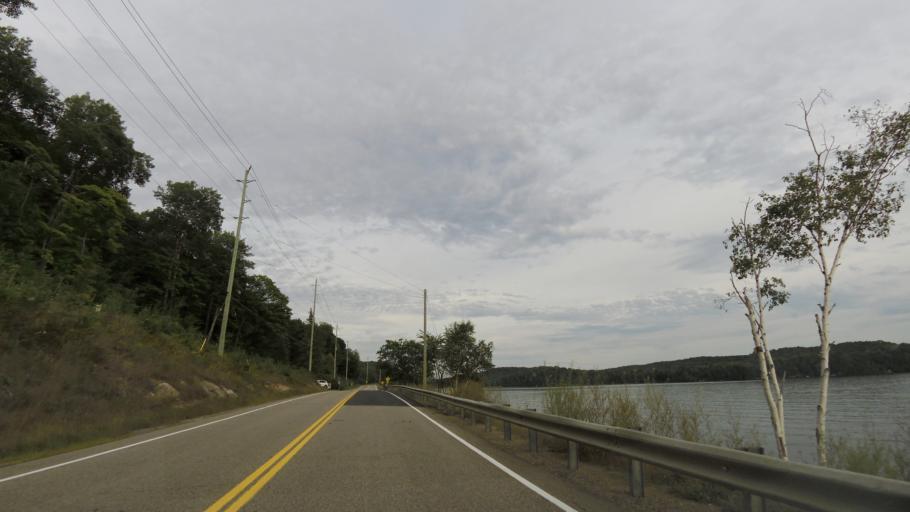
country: CA
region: Ontario
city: Bancroft
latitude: 45.0229
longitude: -78.3788
